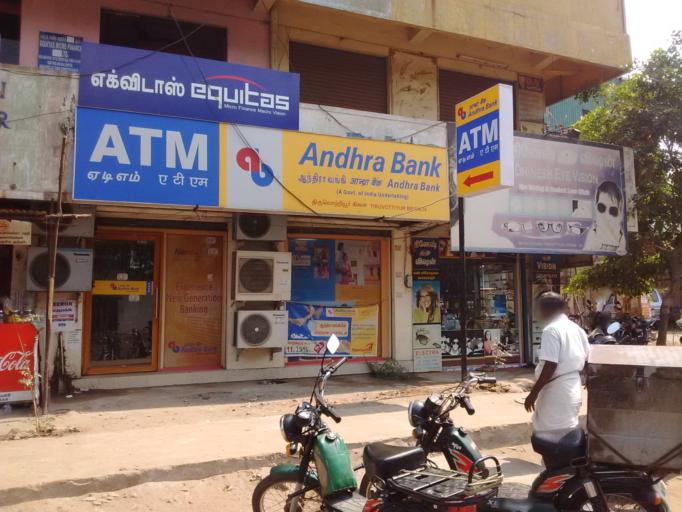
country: IN
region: Tamil Nadu
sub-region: Thiruvallur
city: Tiruvottiyur
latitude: 13.1707
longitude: 80.3050
